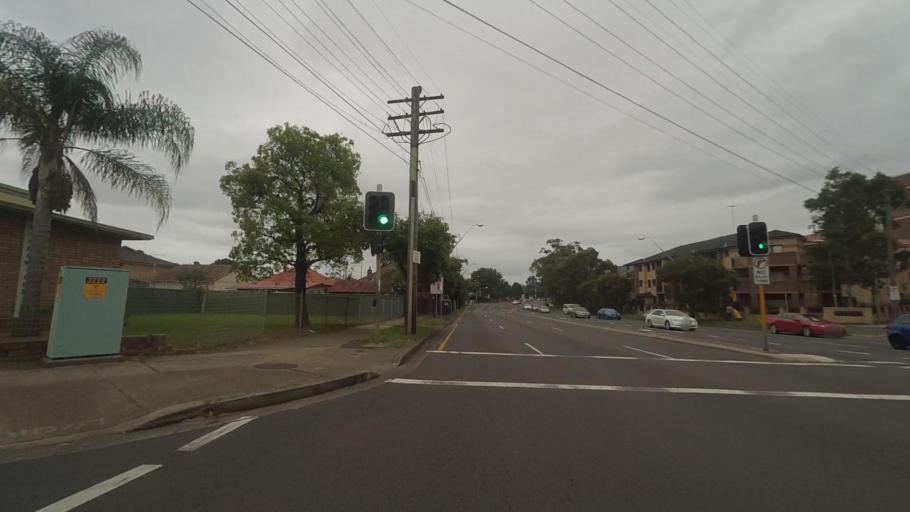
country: AU
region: New South Wales
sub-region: Auburn
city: Lidcombe
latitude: -33.8664
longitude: 151.0413
